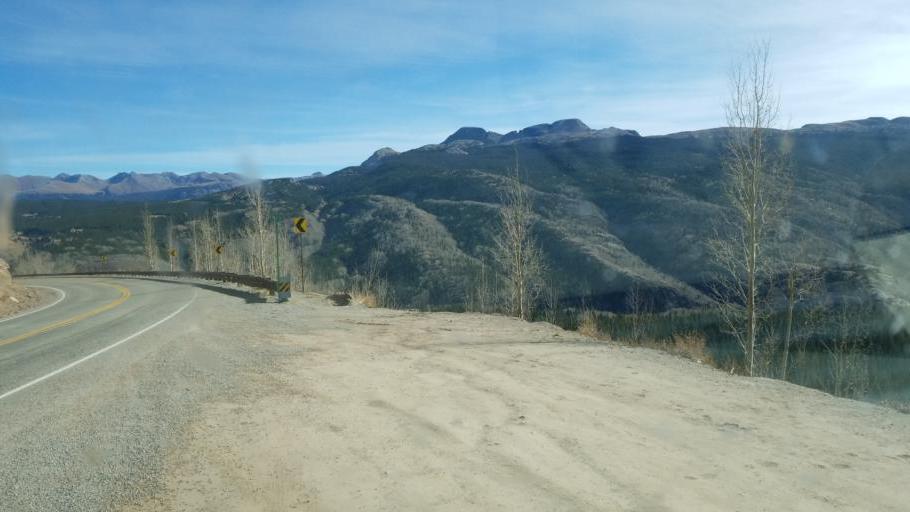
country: US
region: Colorado
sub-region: San Juan County
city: Silverton
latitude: 37.7007
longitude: -107.7701
